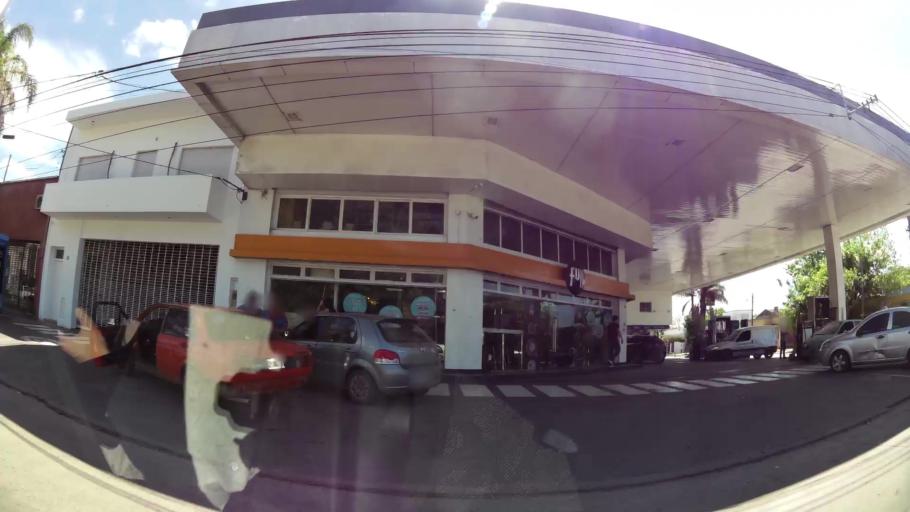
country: AR
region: Buenos Aires
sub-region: Partido de Quilmes
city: Quilmes
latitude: -34.8142
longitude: -58.2776
